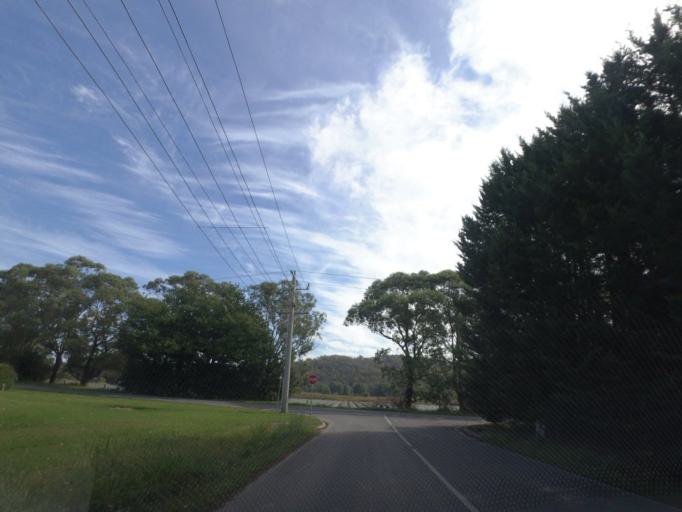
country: AU
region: Victoria
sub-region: Yarra Ranges
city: Healesville
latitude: -37.6433
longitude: 145.5247
